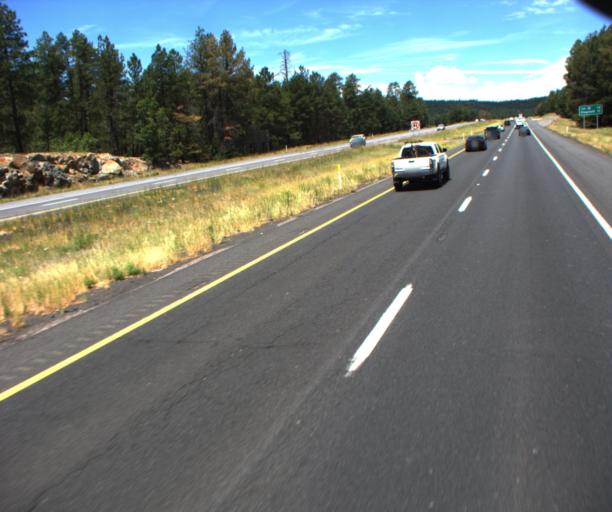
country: US
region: Arizona
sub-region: Coconino County
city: Sedona
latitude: 34.9499
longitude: -111.6654
